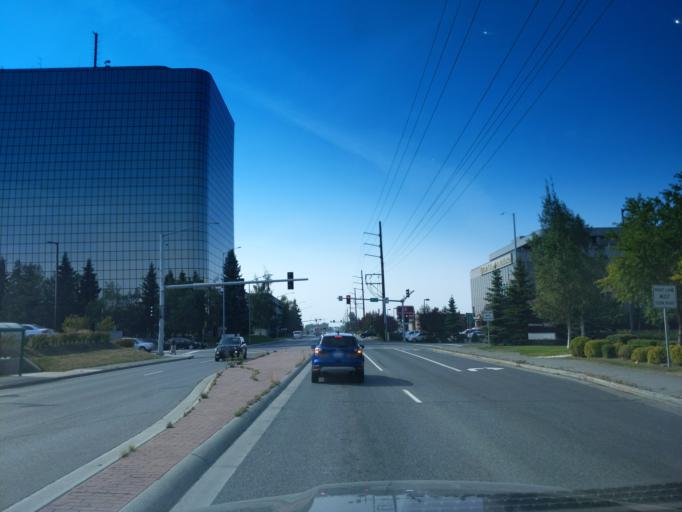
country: US
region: Alaska
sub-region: Anchorage Municipality
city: Anchorage
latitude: 61.1881
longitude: -149.8819
